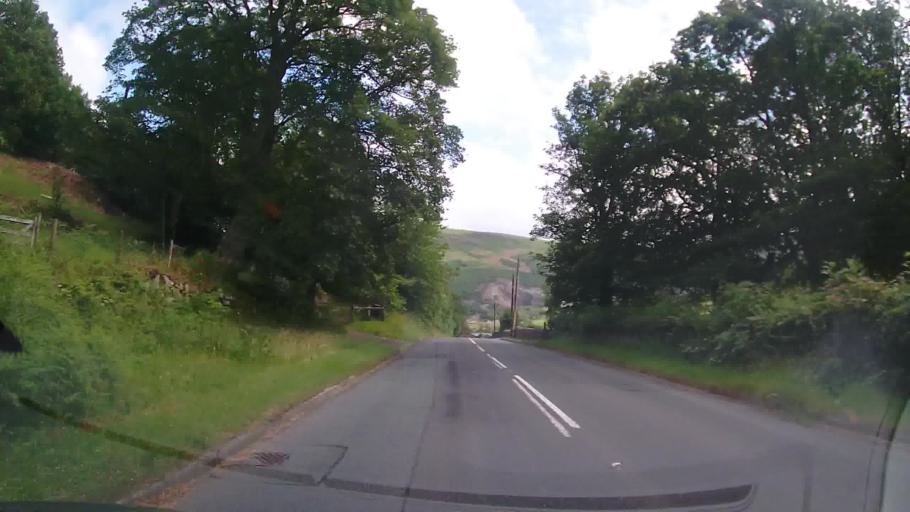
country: GB
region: Wales
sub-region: Sir Powys
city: Llangynog
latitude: 52.8303
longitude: -3.4134
